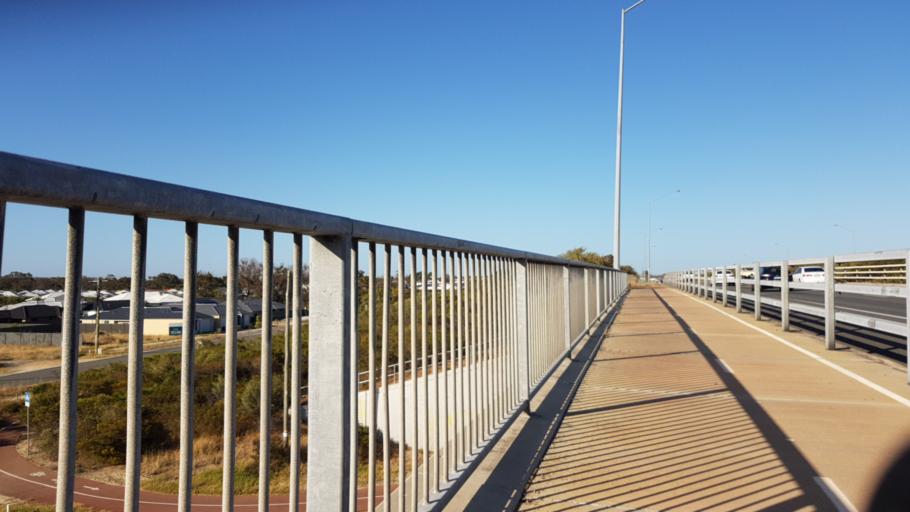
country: AU
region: Western Australia
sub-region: Kwinana
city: Wellard
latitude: -32.2720
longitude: 115.8444
